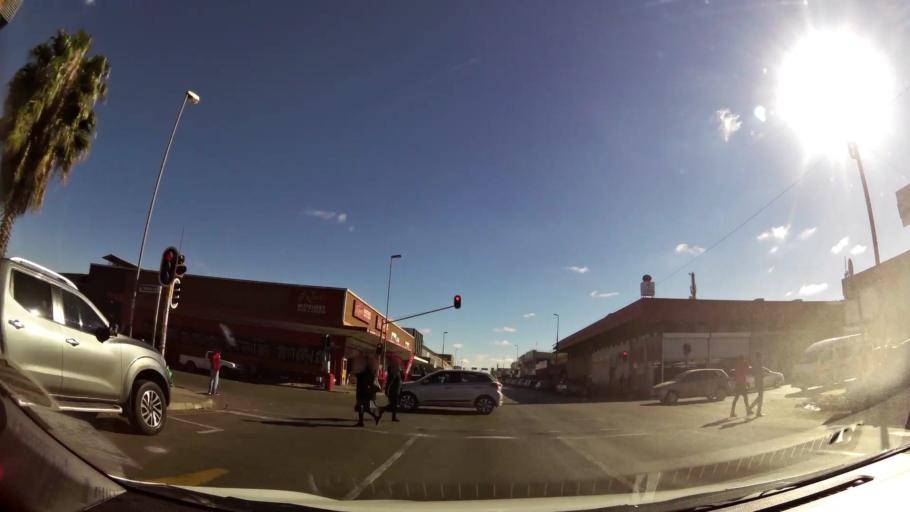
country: ZA
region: Limpopo
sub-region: Capricorn District Municipality
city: Polokwane
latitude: -23.9073
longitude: 29.4511
